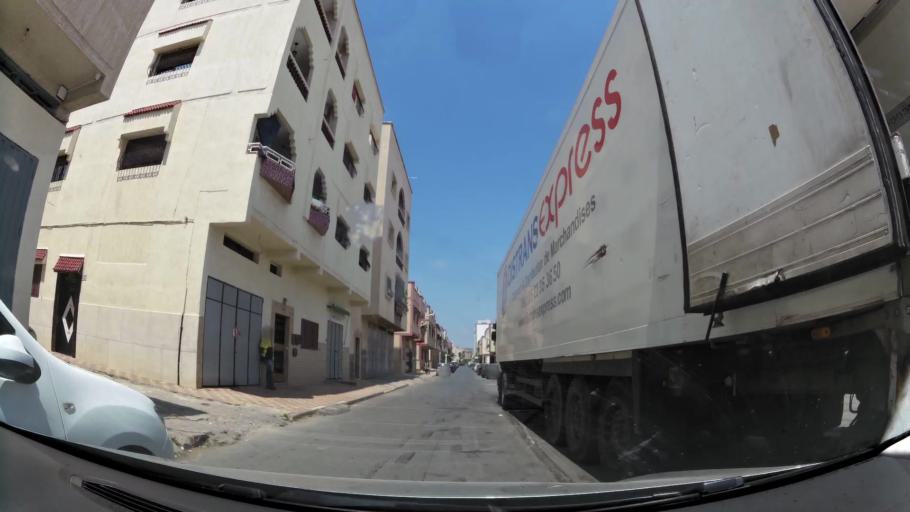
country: MA
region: Rabat-Sale-Zemmour-Zaer
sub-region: Skhirate-Temara
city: Temara
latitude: 33.9760
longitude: -6.8904
